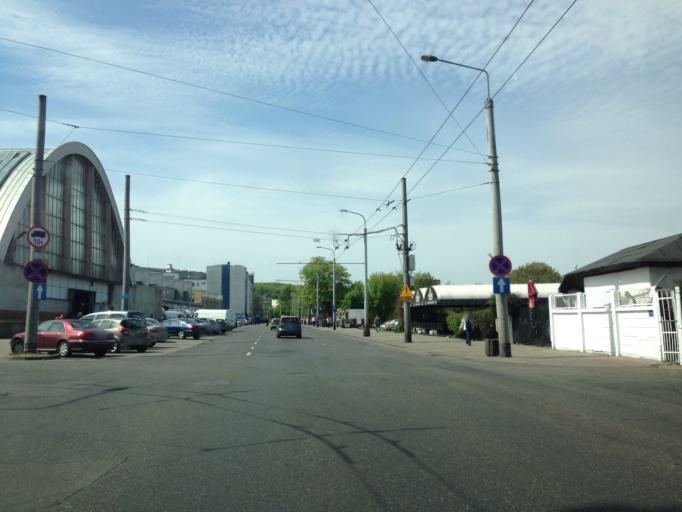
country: PL
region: Pomeranian Voivodeship
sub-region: Gdynia
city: Gdynia
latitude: 54.5233
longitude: 18.5355
